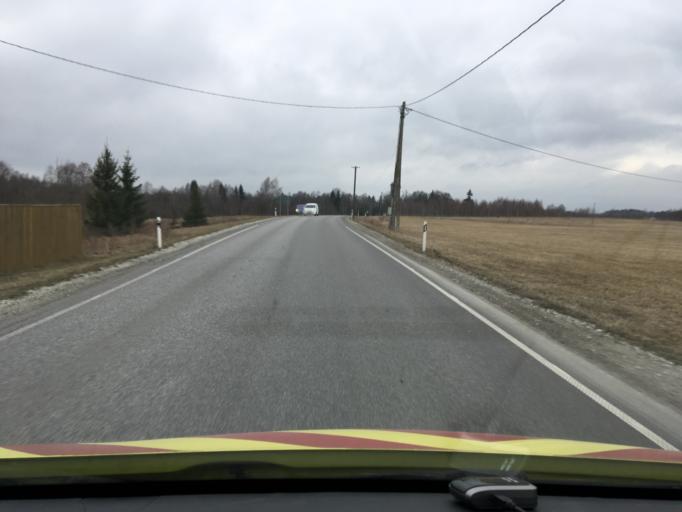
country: EE
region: Raplamaa
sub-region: Rapla vald
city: Rapla
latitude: 58.9964
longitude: 24.8474
